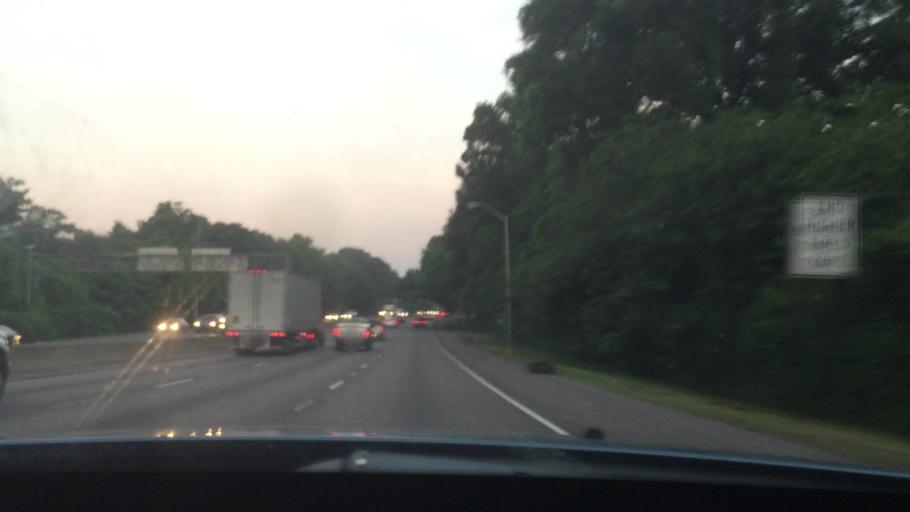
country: US
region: Louisiana
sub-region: East Baton Rouge Parish
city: Baton Rouge
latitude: 30.4254
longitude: -91.1613
